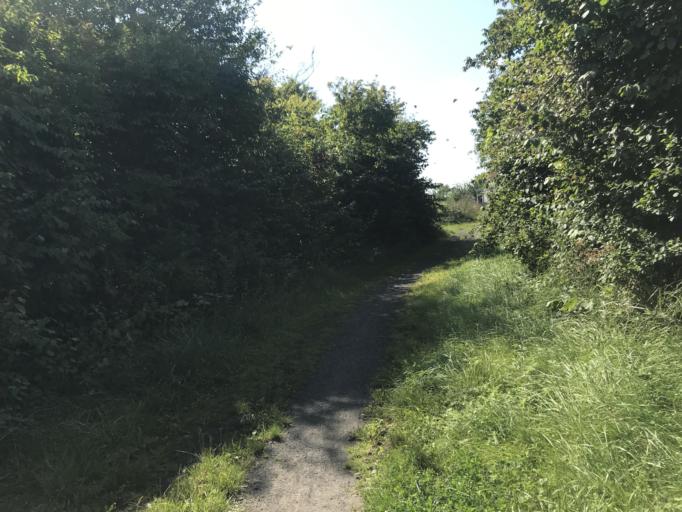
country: DE
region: Hesse
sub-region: Regierungsbezirk Giessen
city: Hungen
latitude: 50.4383
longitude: 8.8906
